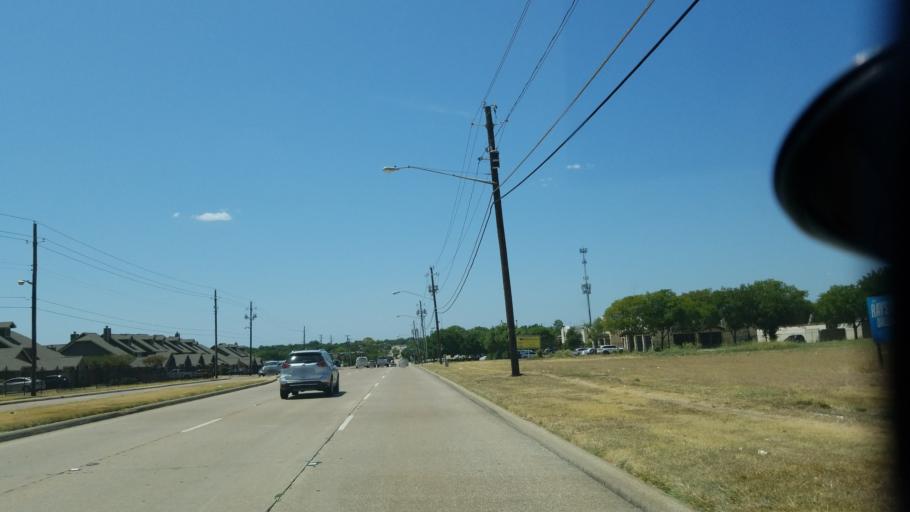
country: US
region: Texas
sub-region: Dallas County
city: Duncanville
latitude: 32.6476
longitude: -96.8886
